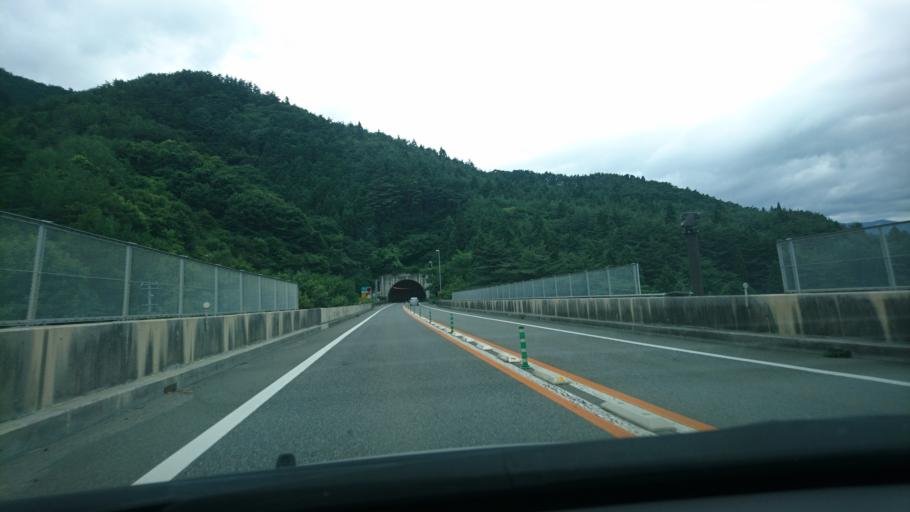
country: JP
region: Iwate
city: Ofunato
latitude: 39.0599
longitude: 141.7102
